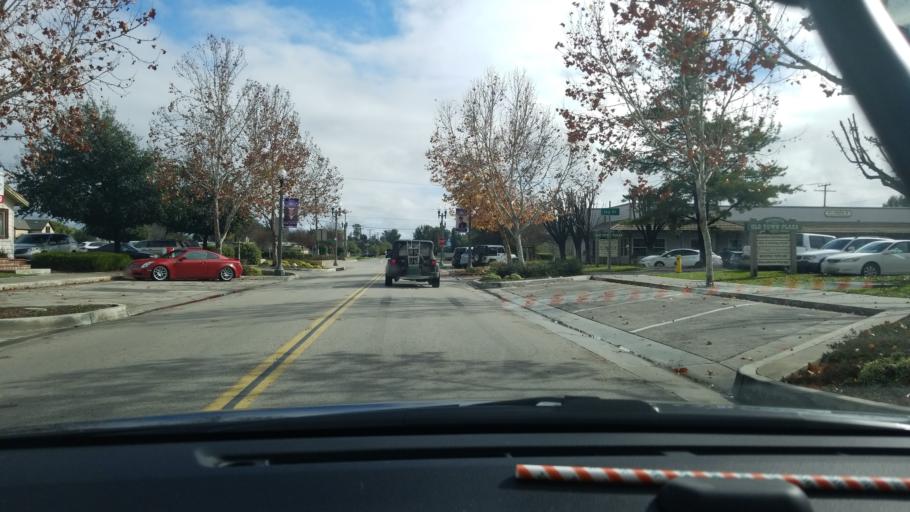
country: US
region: California
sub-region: Riverside County
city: Murrieta
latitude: 33.5516
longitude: -117.2119
